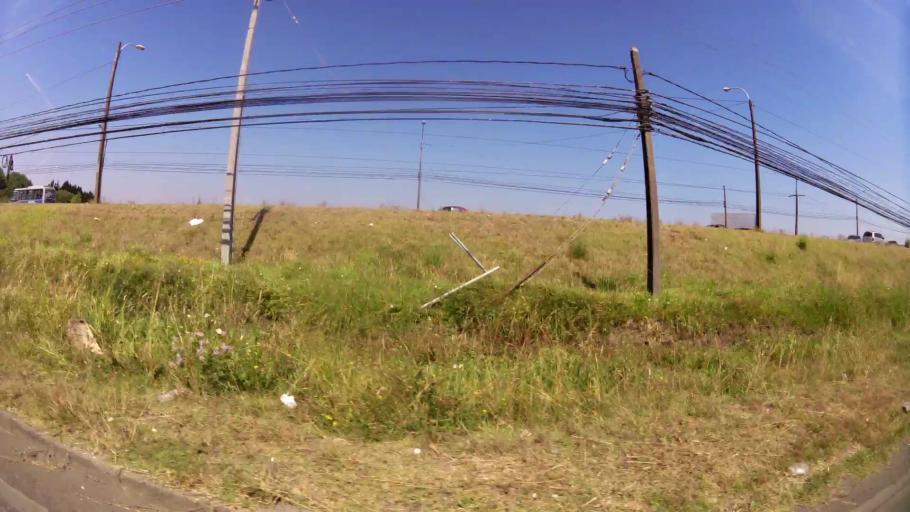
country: CL
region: Biobio
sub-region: Provincia de Concepcion
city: Concepcion
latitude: -36.8024
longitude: -73.0736
